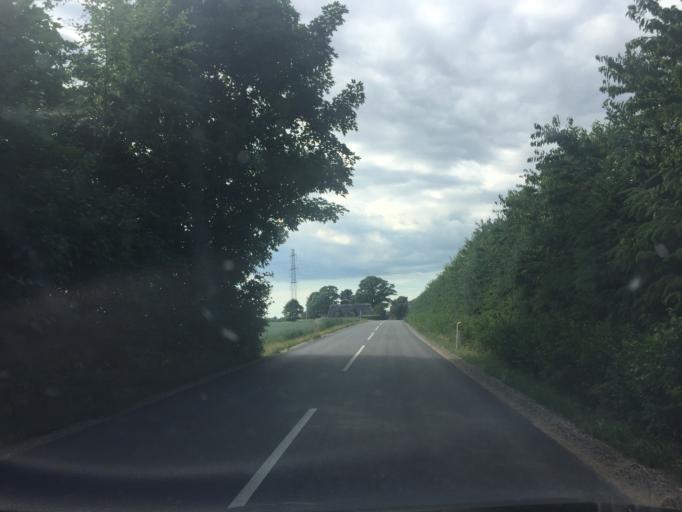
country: DK
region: Capital Region
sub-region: Egedal Kommune
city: Vekso
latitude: 55.7052
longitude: 12.2273
